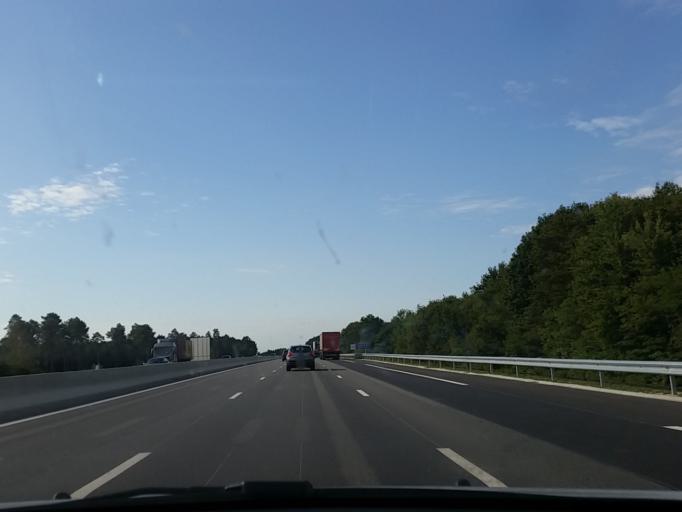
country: FR
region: Centre
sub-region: Departement du Loir-et-Cher
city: Theillay
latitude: 47.2762
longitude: 2.0427
